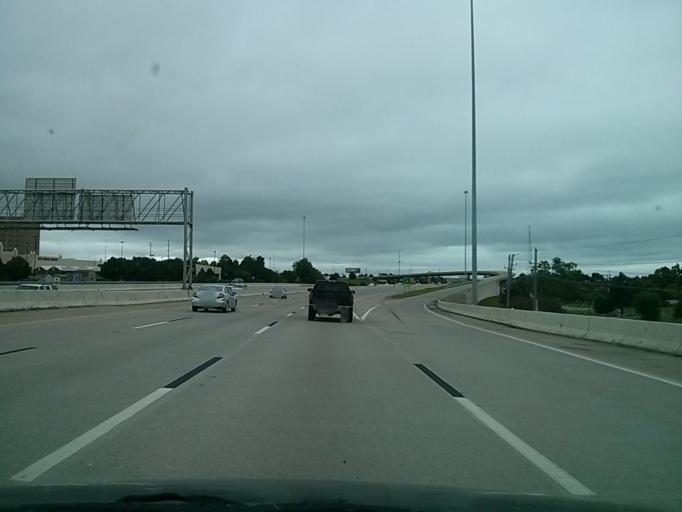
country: US
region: Oklahoma
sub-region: Tulsa County
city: Tulsa
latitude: 36.1478
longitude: -95.9798
